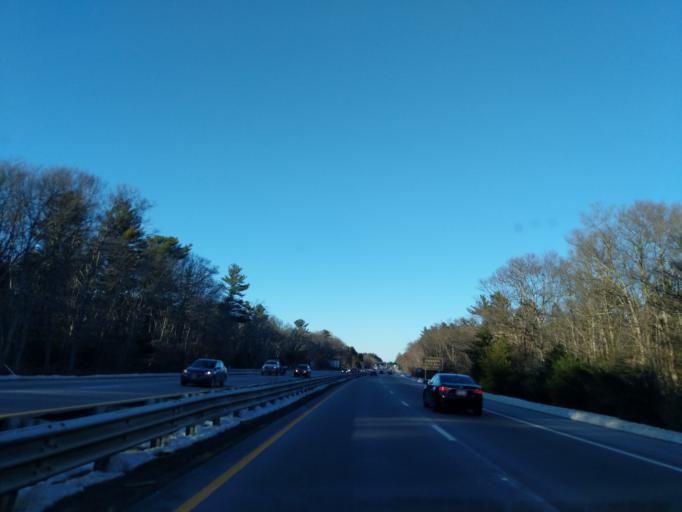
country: US
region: Massachusetts
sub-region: Bristol County
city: Raynham Center
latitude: 41.8976
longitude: -71.0477
